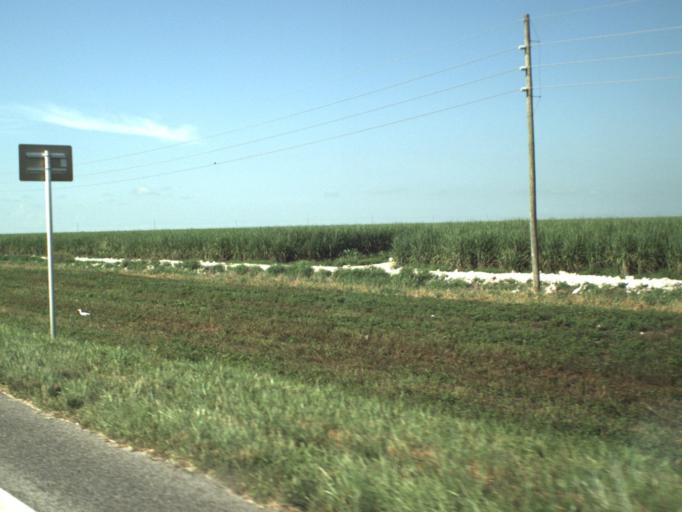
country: US
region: Florida
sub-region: Palm Beach County
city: Belle Glade Camp
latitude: 26.5886
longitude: -80.7112
